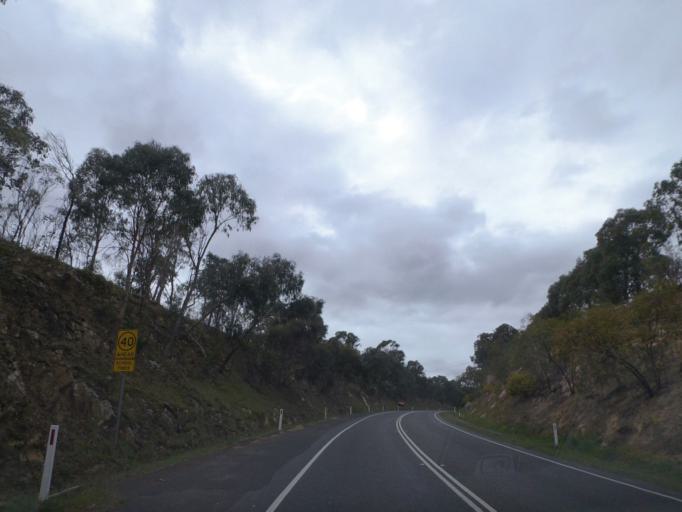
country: AU
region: Victoria
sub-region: Nillumbik
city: Eltham
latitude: -37.7477
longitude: 145.1801
